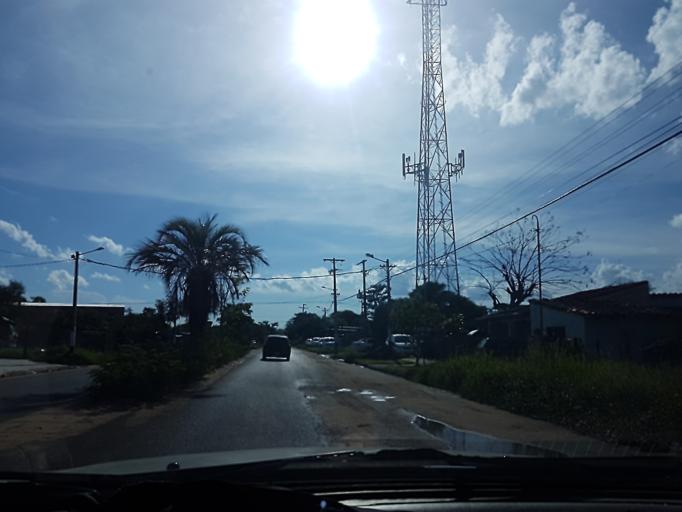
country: PY
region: Central
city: Limpio
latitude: -25.1757
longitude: -57.4787
